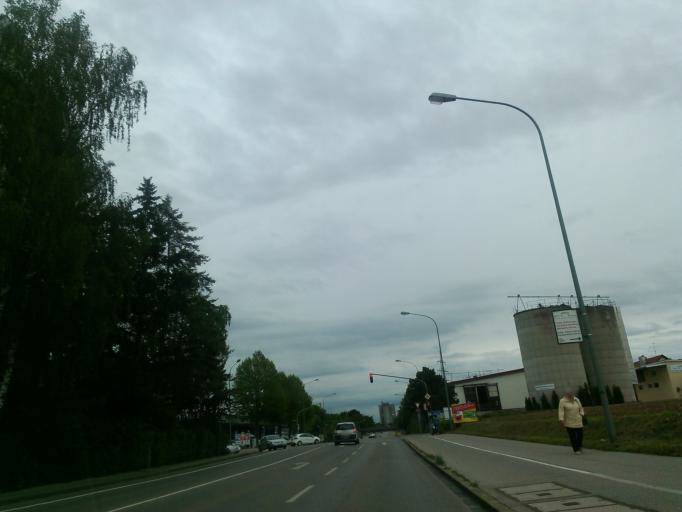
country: DE
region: Bavaria
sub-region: Swabia
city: Augsburg
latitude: 48.3377
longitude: 10.8816
